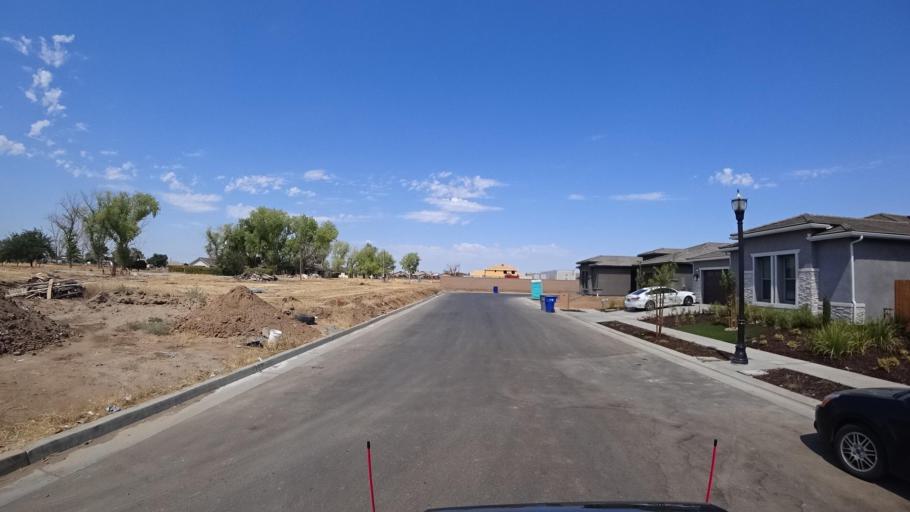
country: US
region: California
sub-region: Fresno County
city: Tarpey Village
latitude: 36.7740
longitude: -119.6747
